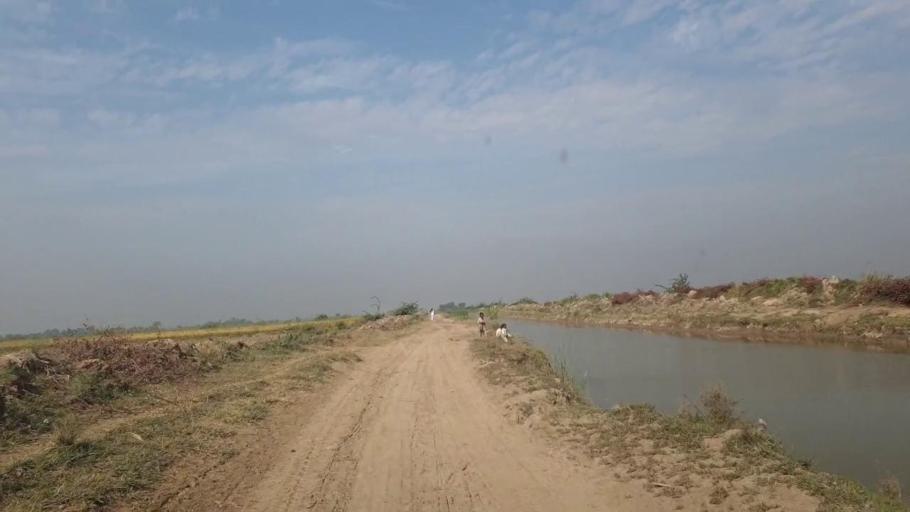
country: PK
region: Sindh
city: Tando Bago
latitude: 24.8725
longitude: 68.9664
